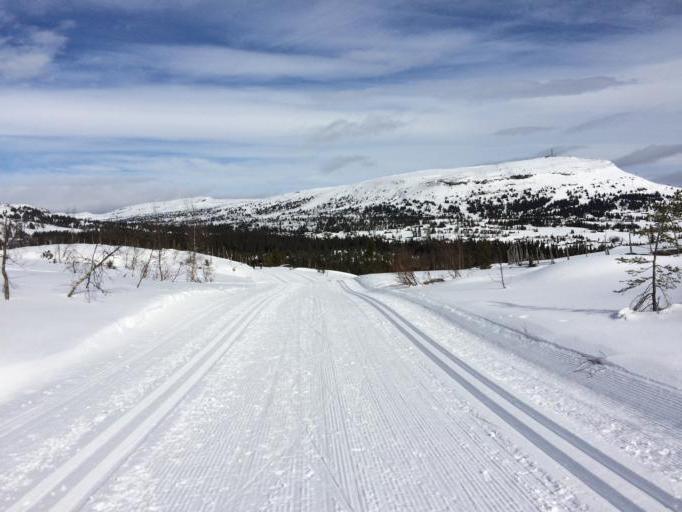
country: NO
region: Oppland
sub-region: Gausdal
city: Segalstad bru
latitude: 61.3337
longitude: 10.0506
